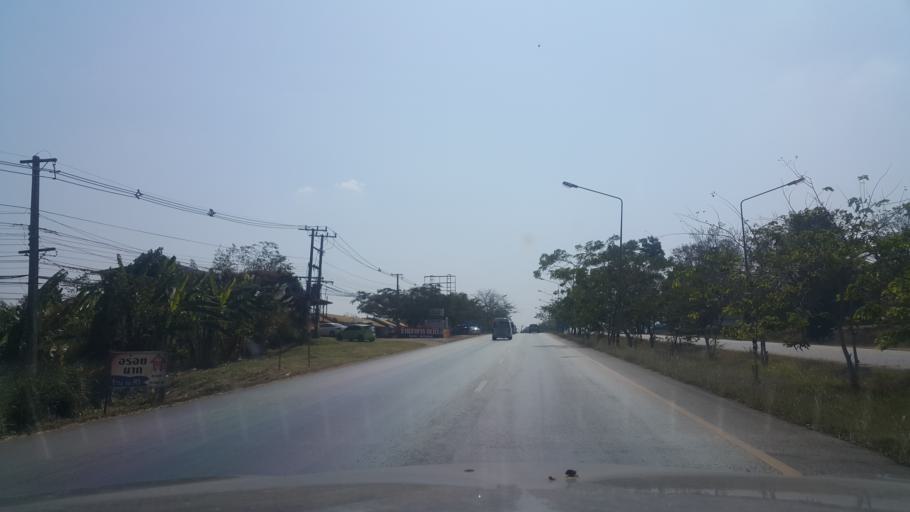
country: TH
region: Nakhon Ratchasima
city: Wang Nam Khiao
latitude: 14.3767
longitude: 101.8683
